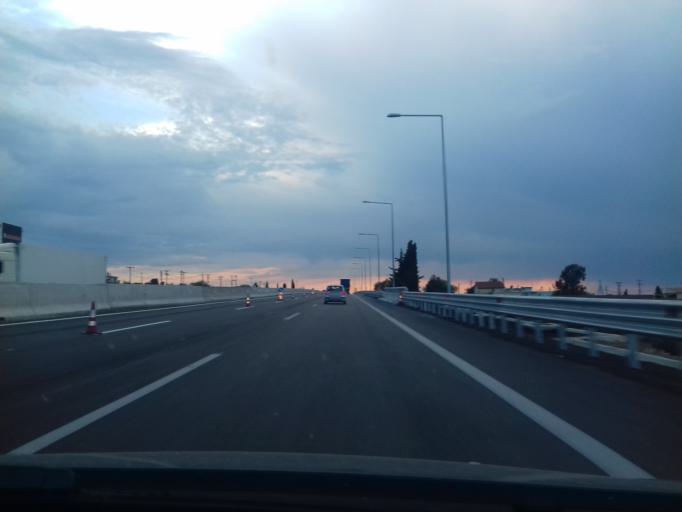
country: GR
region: West Greece
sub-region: Nomos Achaias
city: Rio
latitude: 38.3121
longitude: 21.8214
